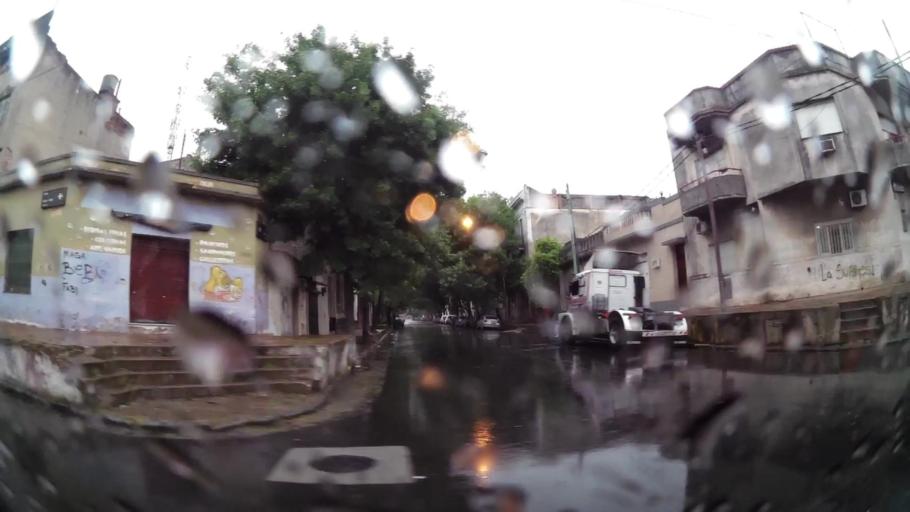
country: AR
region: Buenos Aires
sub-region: Partido de Avellaneda
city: Avellaneda
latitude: -34.6415
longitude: -58.3659
